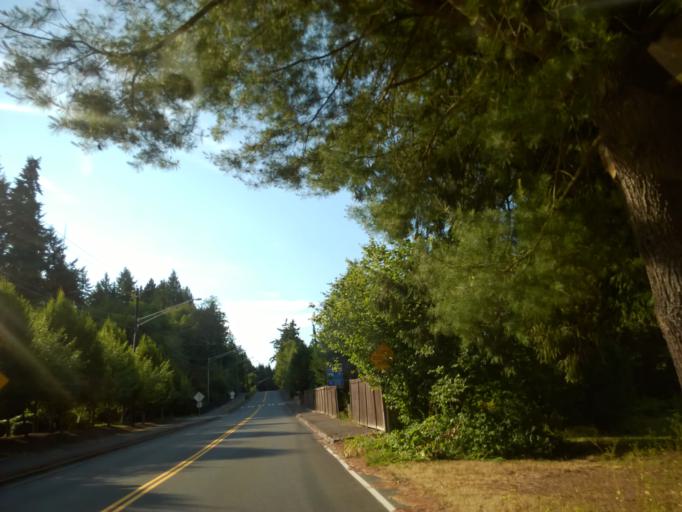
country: US
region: Washington
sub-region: King County
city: Bothell
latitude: 47.7807
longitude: -122.1917
